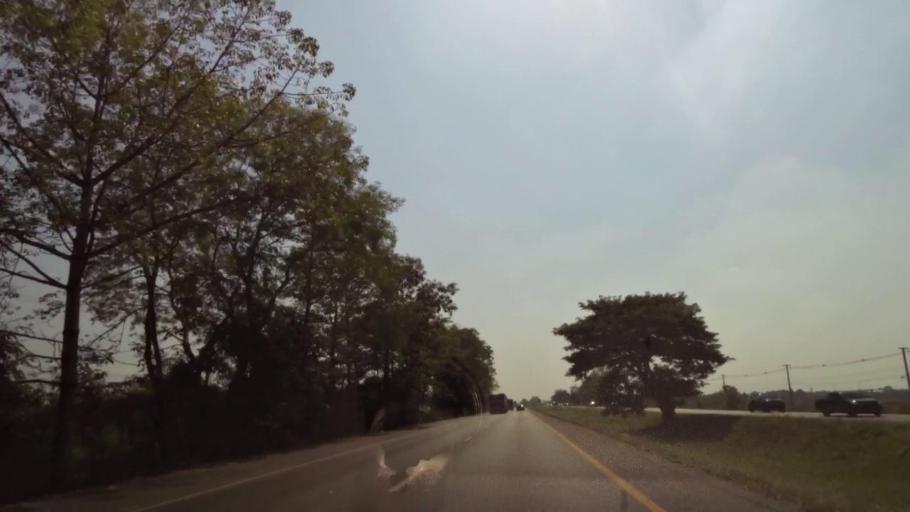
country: TH
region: Phichit
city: Wachira Barami
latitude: 16.4803
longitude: 100.1469
